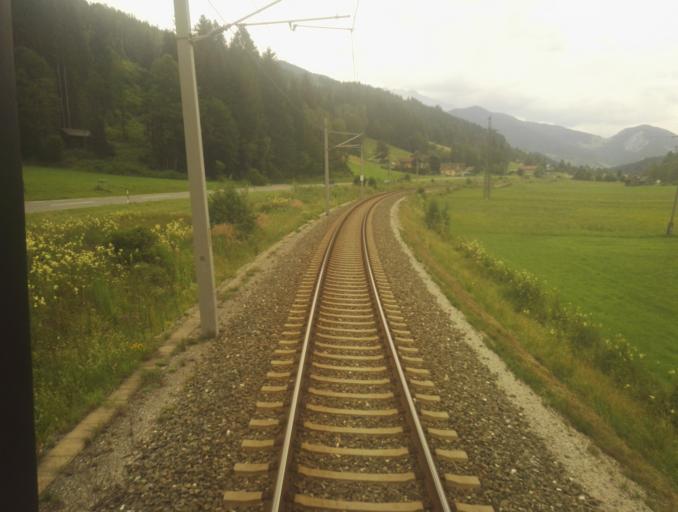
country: AT
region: Salzburg
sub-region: Politischer Bezirk Sankt Johann im Pongau
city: Forstau
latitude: 47.3944
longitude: 13.5134
